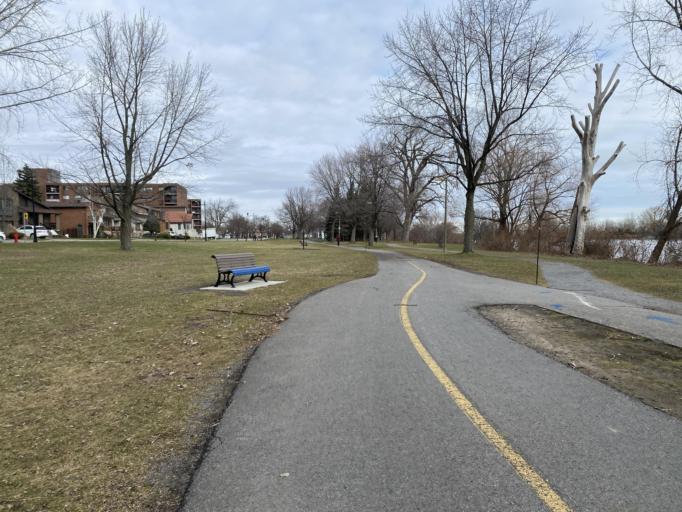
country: CA
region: Quebec
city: Saint-Raymond
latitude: 45.4245
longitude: -73.5973
